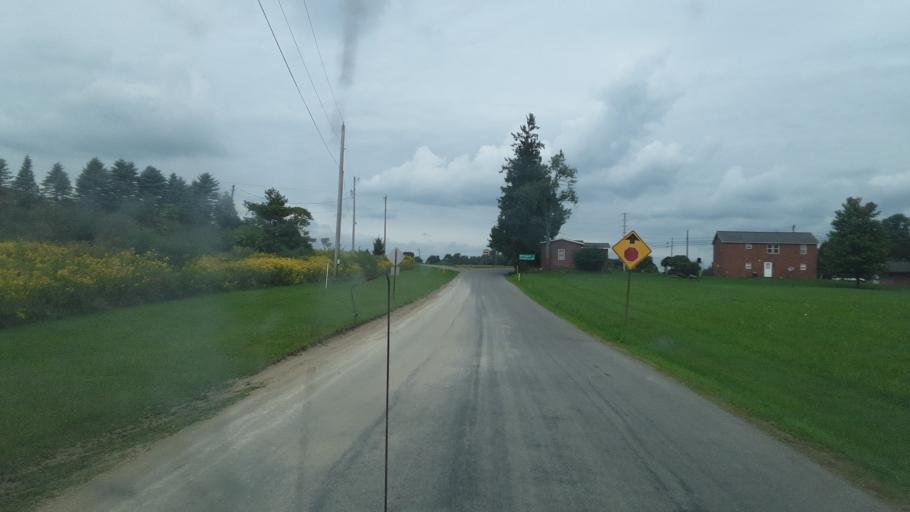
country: US
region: Pennsylvania
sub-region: Jefferson County
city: Punxsutawney
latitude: 40.9638
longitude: -79.0985
